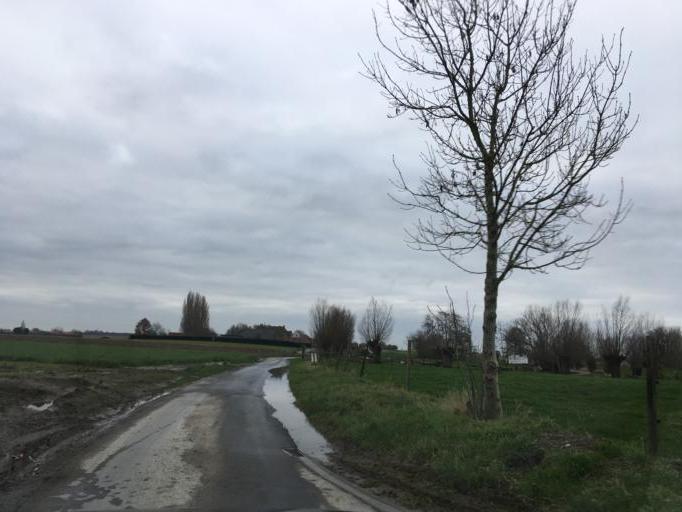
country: BE
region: Flanders
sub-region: Provincie West-Vlaanderen
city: Ledegem
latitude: 50.8995
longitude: 3.1310
